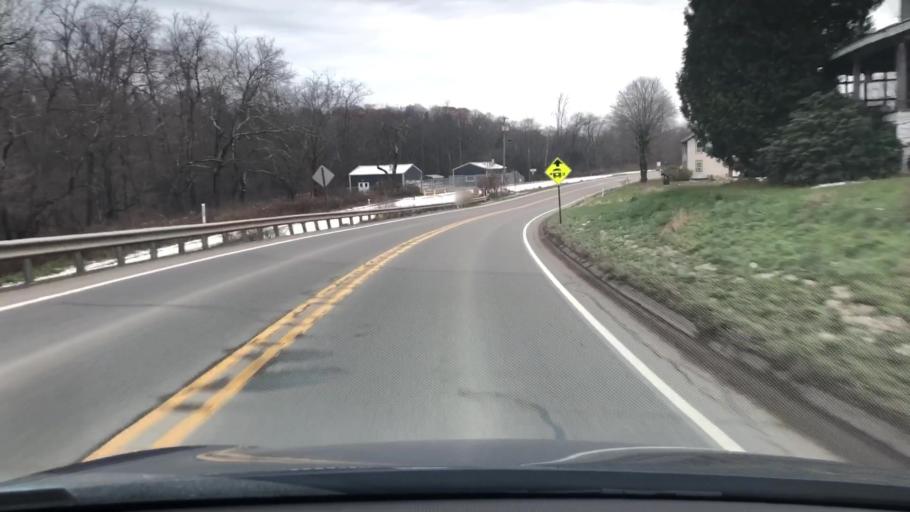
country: US
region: Pennsylvania
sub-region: Clarion County
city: Clarion
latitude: 41.0113
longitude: -79.2836
